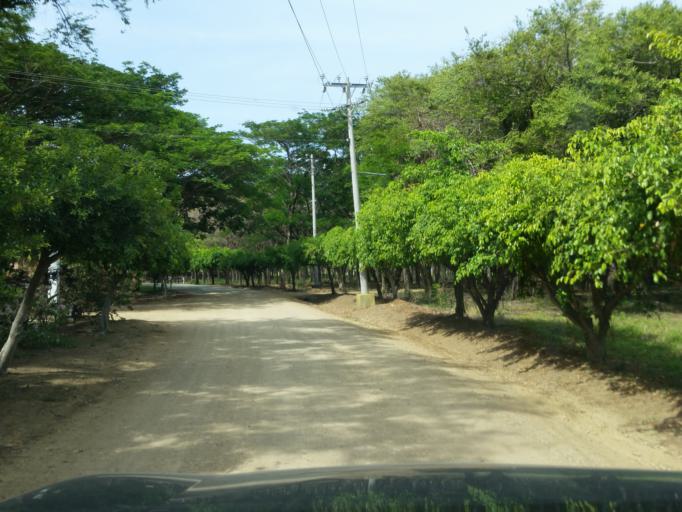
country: NI
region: Rivas
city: Tola
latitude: 11.4137
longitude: -86.0513
